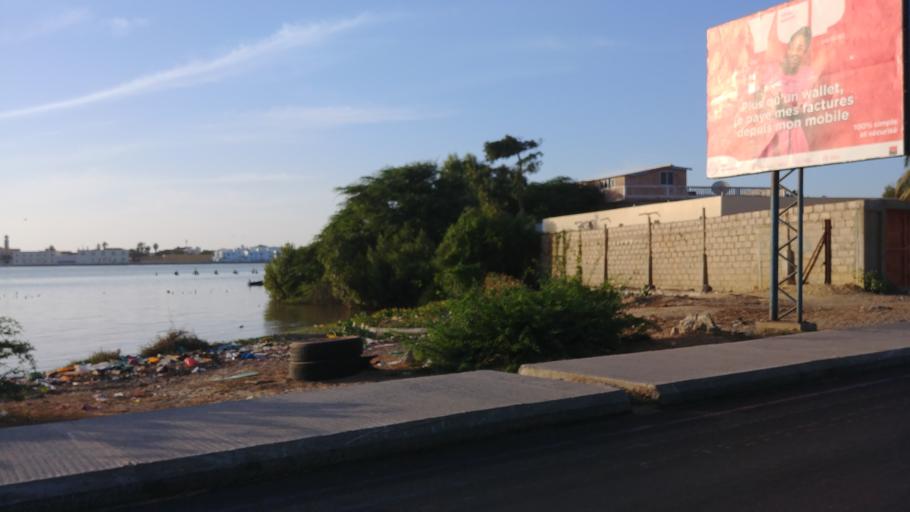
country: SN
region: Saint-Louis
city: Saint-Louis
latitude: 16.0177
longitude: -16.4996
